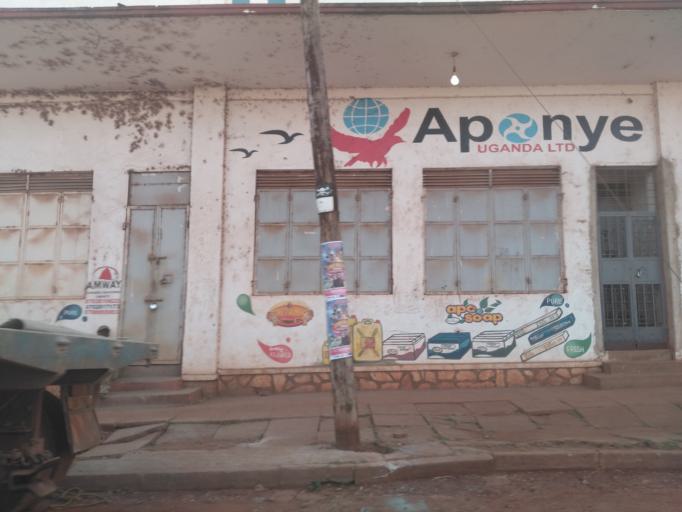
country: UG
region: Eastern Region
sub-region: Jinja District
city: Jinja
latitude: 0.4273
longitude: 33.2118
